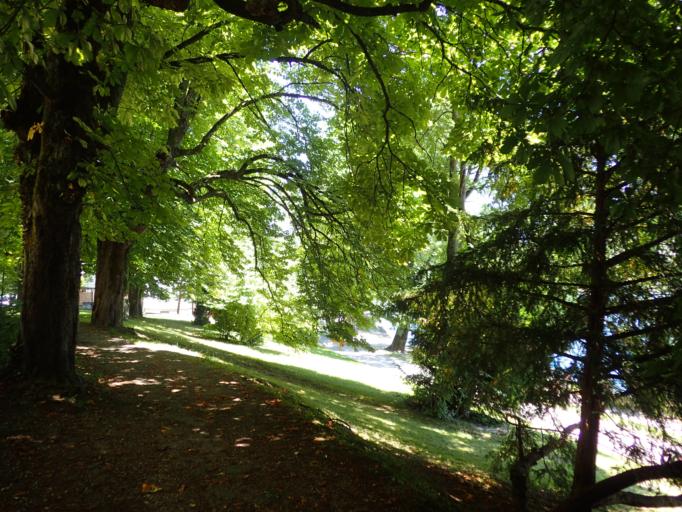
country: SI
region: Bled
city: Bled
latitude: 46.3695
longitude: 14.1040
